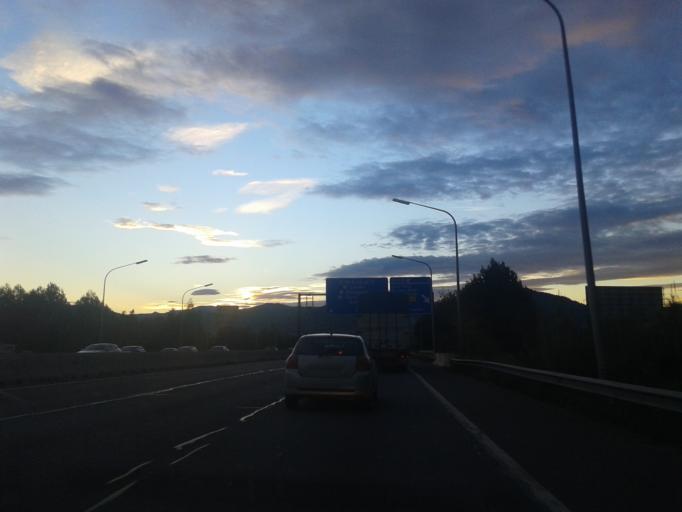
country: ES
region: Catalonia
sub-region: Provincia de Barcelona
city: Sant Feliu de Llobregat
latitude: 41.3744
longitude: 2.0576
